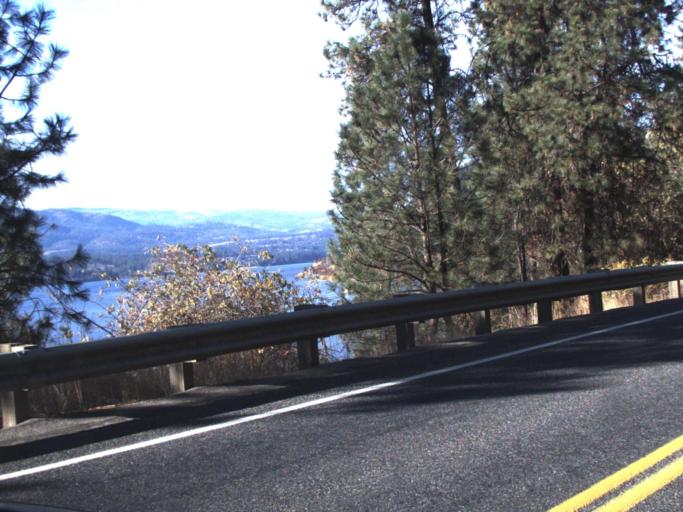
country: US
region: Washington
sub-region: Stevens County
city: Kettle Falls
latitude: 48.6242
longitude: -118.0725
